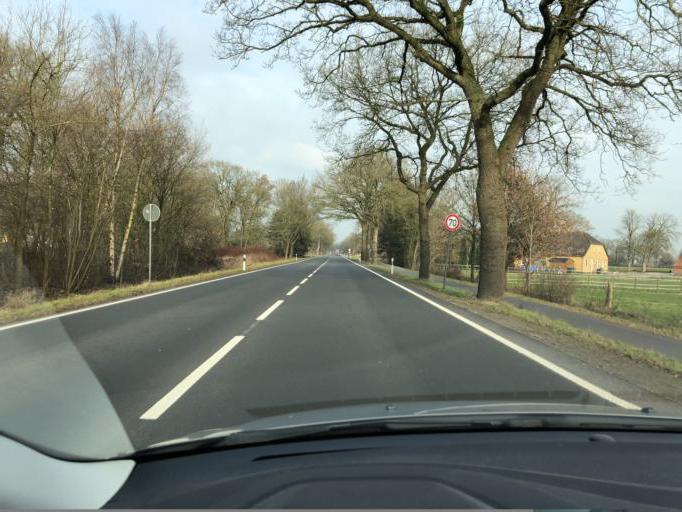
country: DE
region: Lower Saxony
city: Hesel
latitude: 53.3517
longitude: 7.6018
